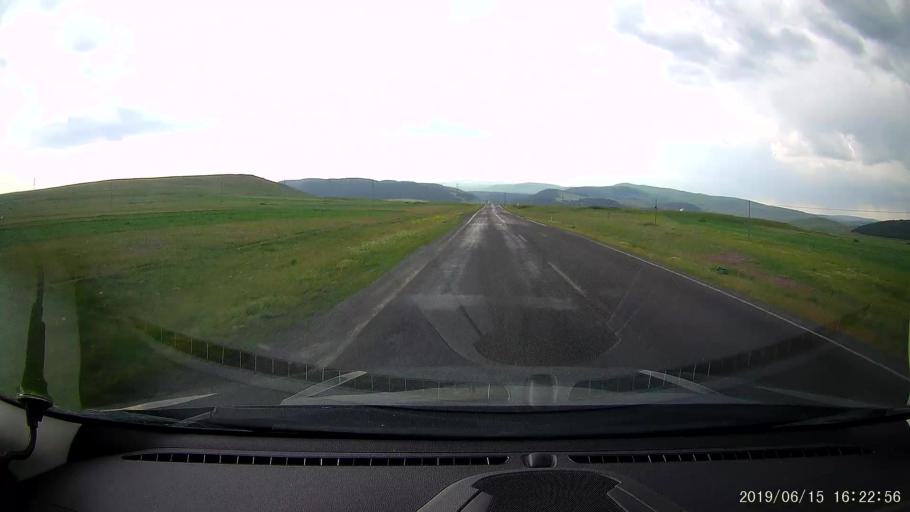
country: TR
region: Ardahan
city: Hanak
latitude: 41.1829
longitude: 42.8561
